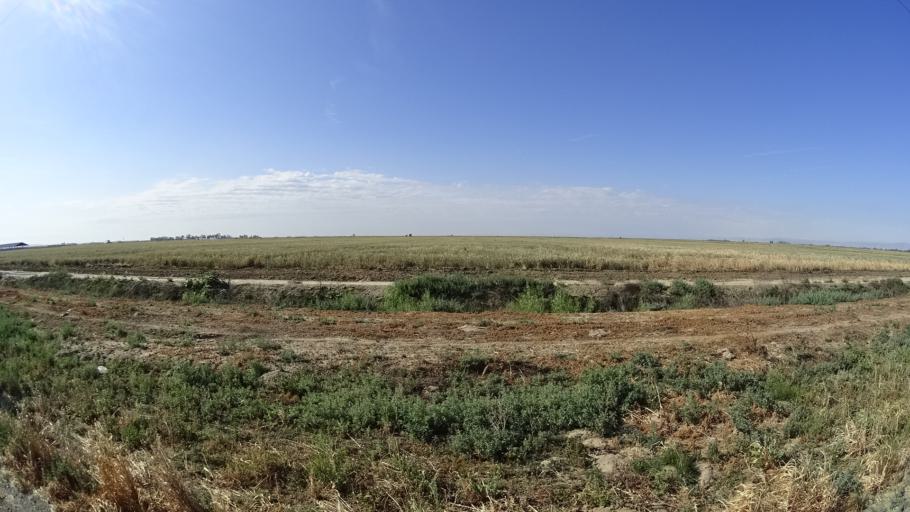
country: US
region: California
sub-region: Kings County
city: Armona
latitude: 36.2256
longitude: -119.7205
